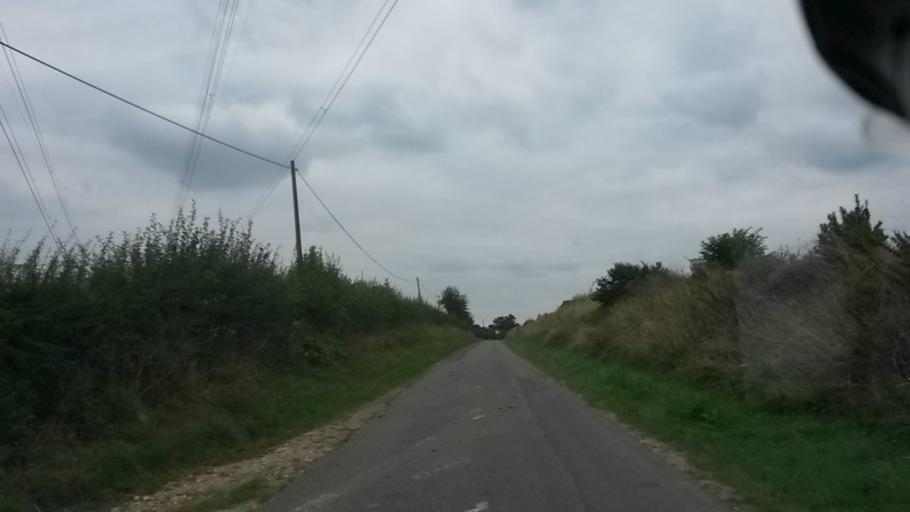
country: FR
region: Haute-Normandie
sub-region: Departement de la Seine-Maritime
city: La Feuillie
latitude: 49.4761
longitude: 1.5292
